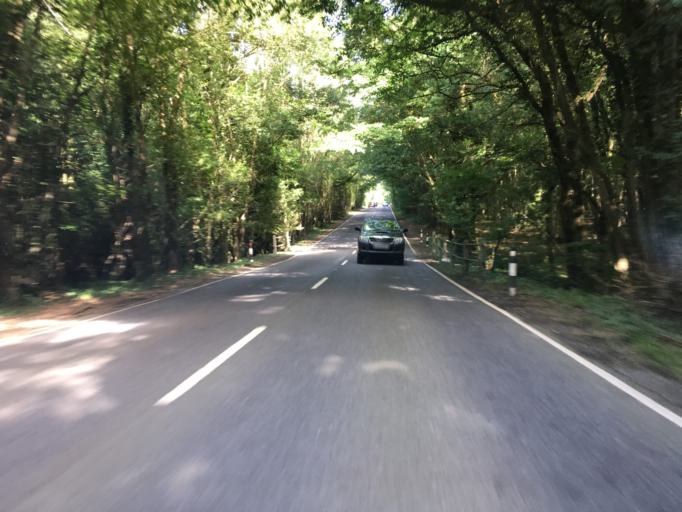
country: GB
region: England
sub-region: West Sussex
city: Billingshurst
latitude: 51.0522
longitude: -0.4111
